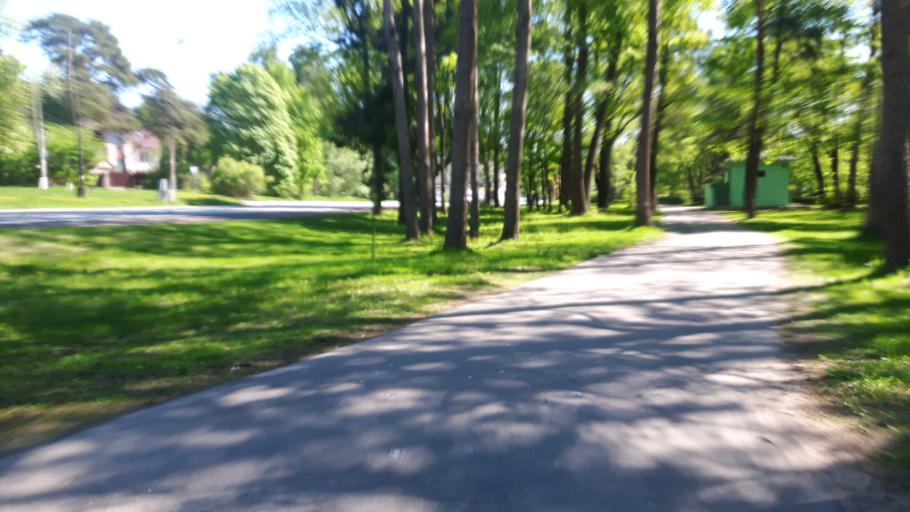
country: RU
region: St.-Petersburg
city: Zelenogorsk
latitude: 60.1928
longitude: 29.6879
